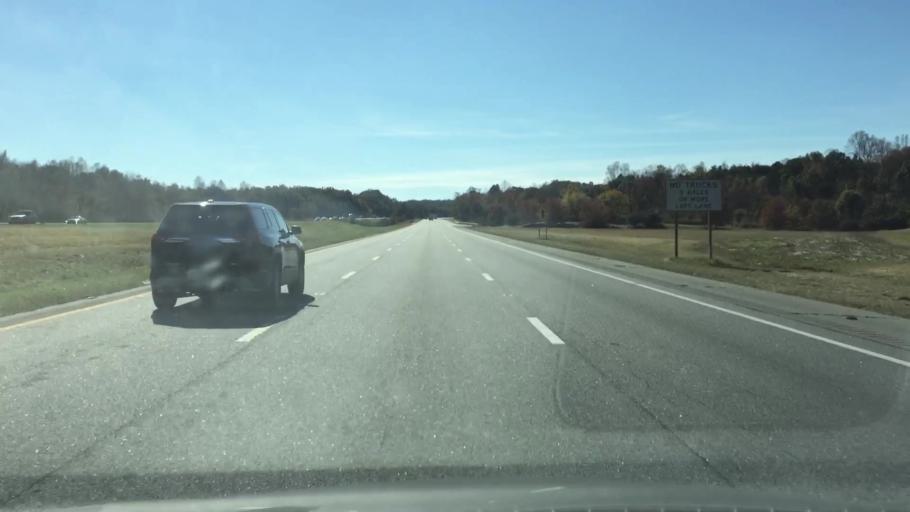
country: US
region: North Carolina
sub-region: Randolph County
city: Trinity
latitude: 35.8800
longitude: -80.0032
